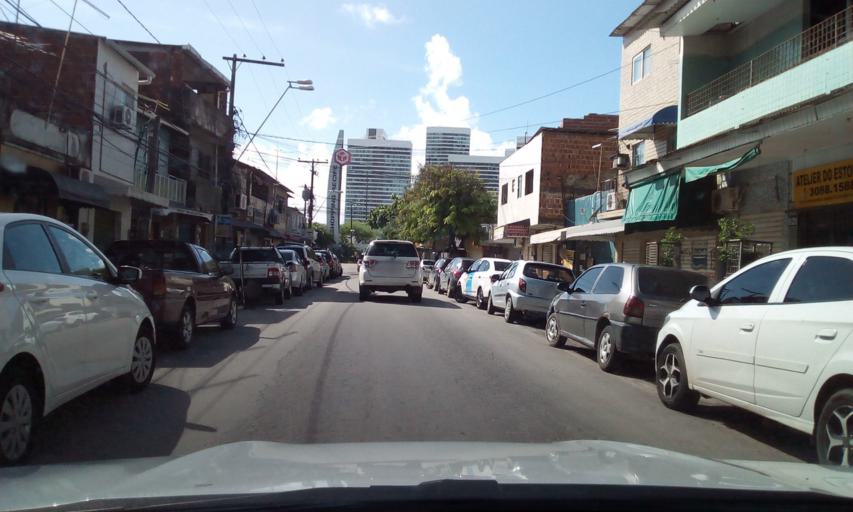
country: BR
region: Pernambuco
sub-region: Recife
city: Recife
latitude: -8.1217
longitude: -34.9040
